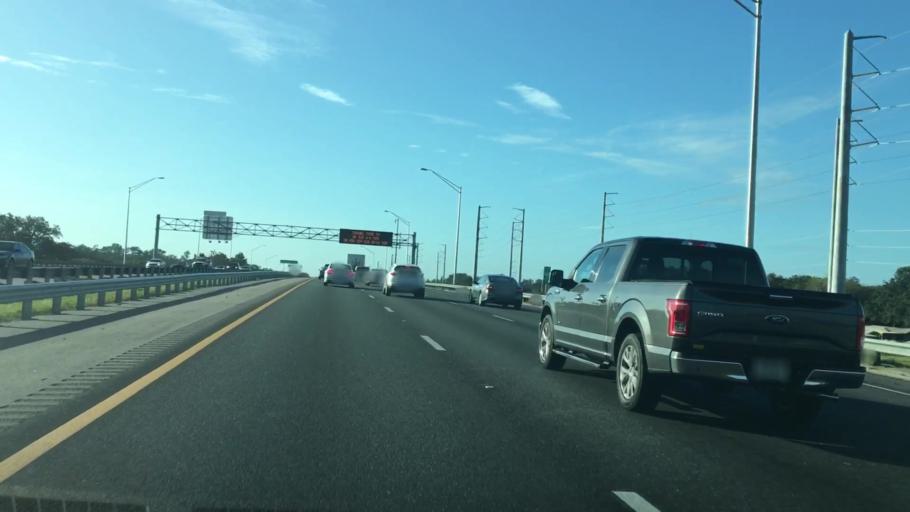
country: US
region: Florida
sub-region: Orange County
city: Azalea Park
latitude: 28.5262
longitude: -81.2509
